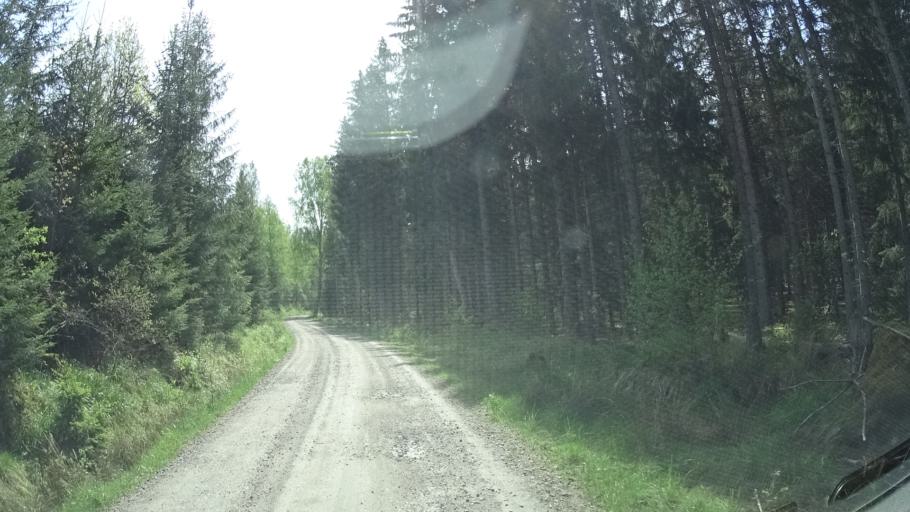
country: SE
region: OEstergoetland
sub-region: Finspangs Kommun
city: Finspang
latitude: 58.7925
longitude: 15.8424
